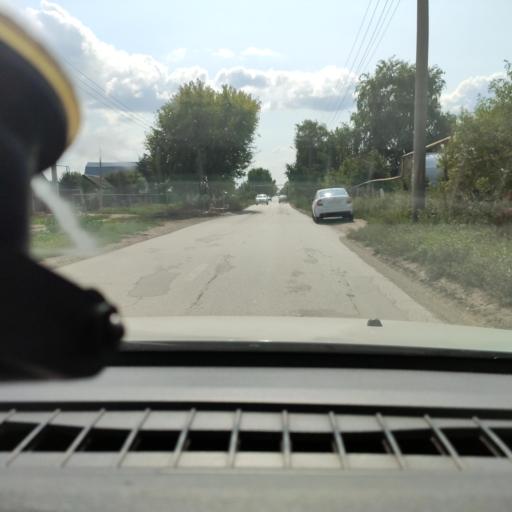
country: RU
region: Samara
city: Chapayevsk
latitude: 53.0090
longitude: 49.7242
